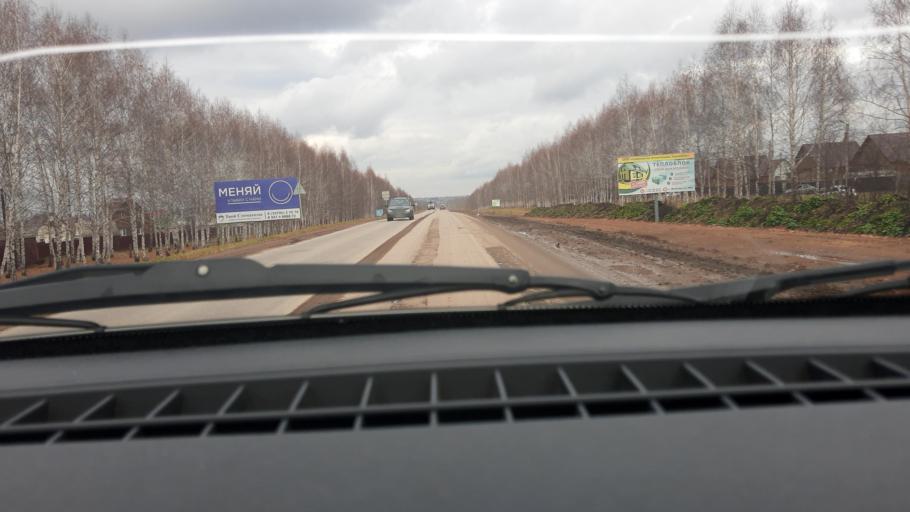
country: RU
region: Bashkortostan
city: Iglino
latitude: 54.8218
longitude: 56.4211
